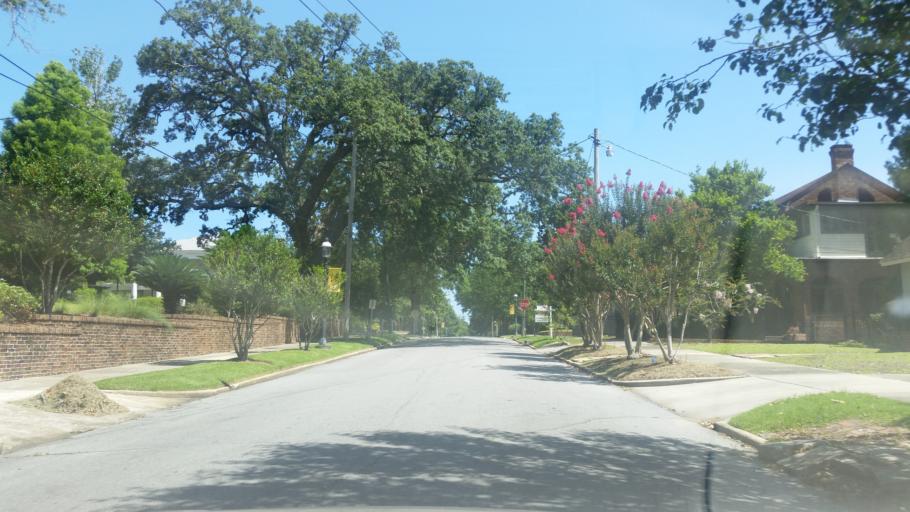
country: US
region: Florida
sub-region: Escambia County
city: Pensacola
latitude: 30.4241
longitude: -87.2208
